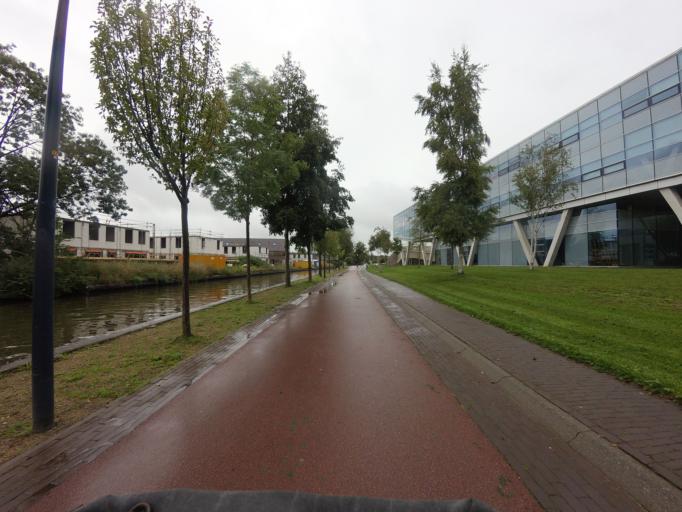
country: NL
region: Friesland
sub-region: Gemeente Leeuwarden
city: Bilgaard
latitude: 53.2119
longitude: 5.8016
